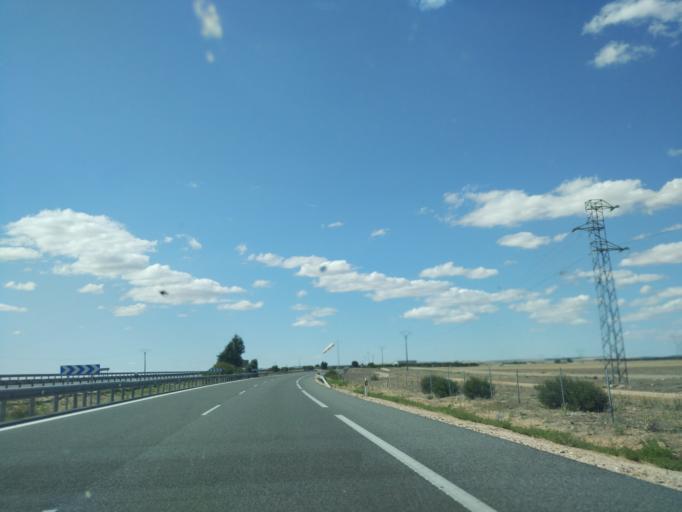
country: ES
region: Castille and Leon
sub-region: Provincia de Valladolid
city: San Vicente del Palacio
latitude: 41.2434
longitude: -4.8650
